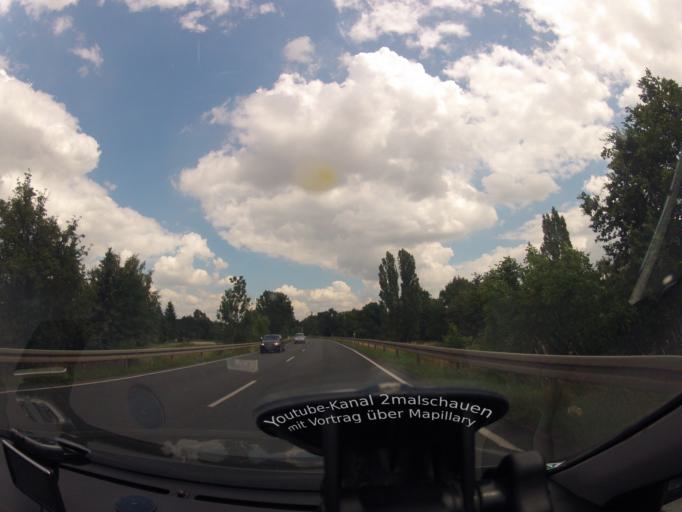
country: DE
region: Saxony
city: Taucha
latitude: 51.3837
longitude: 12.4967
